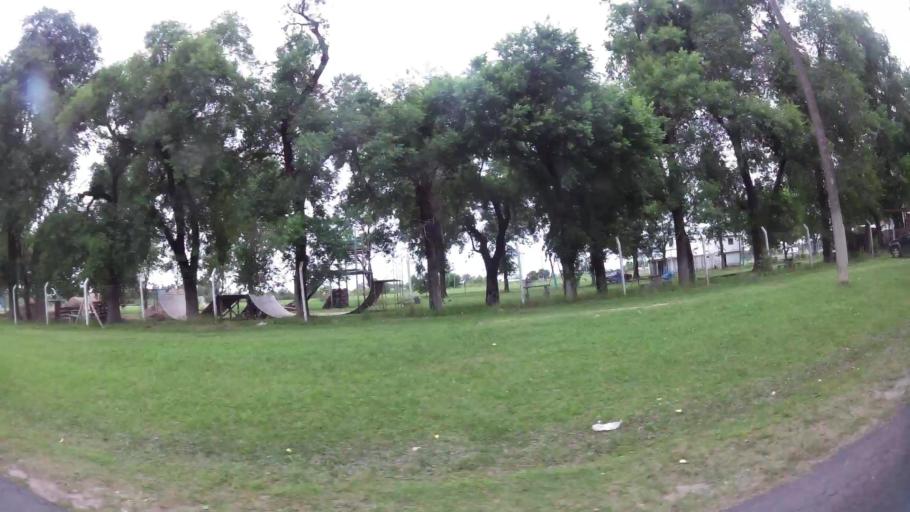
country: AR
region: Buenos Aires
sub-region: Partido de Zarate
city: Zarate
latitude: -34.1171
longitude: -59.0157
